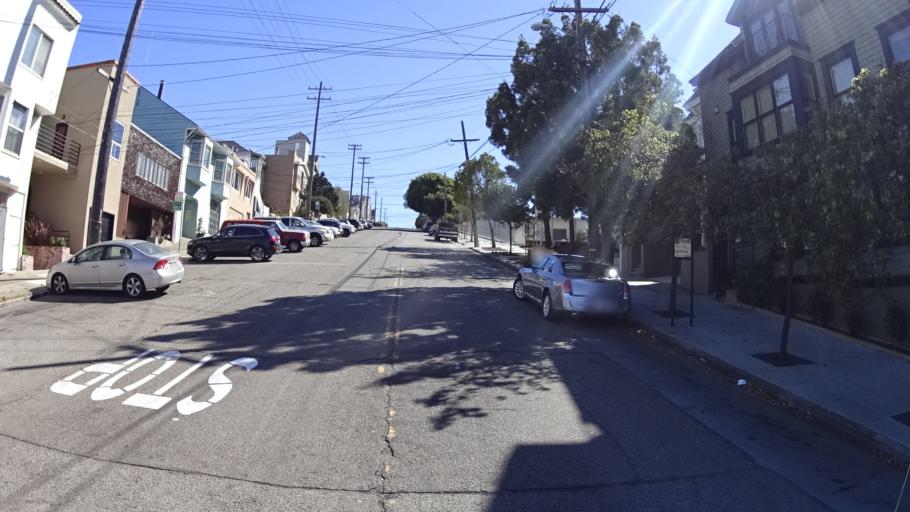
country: US
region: California
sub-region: San Francisco County
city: San Francisco
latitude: 37.7621
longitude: -122.4033
